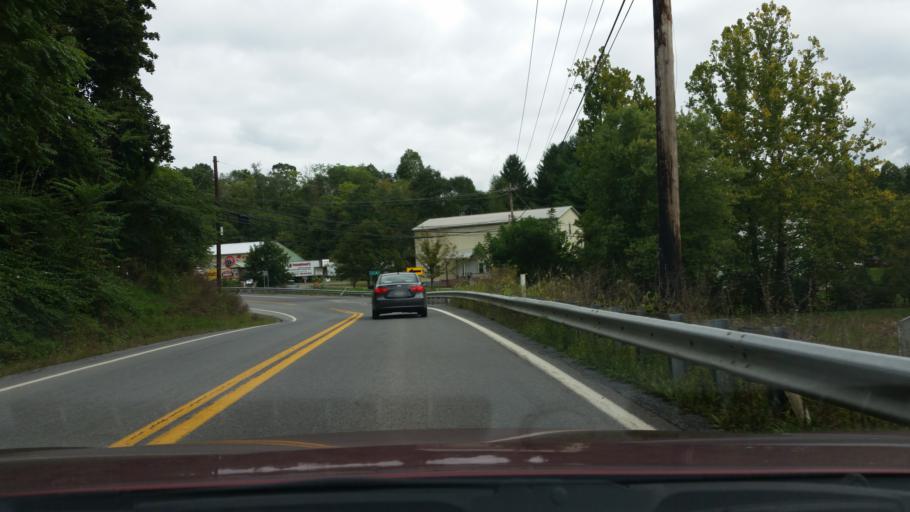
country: US
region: West Virginia
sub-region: Morgan County
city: Berkeley Springs
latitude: 39.6186
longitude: -78.2157
